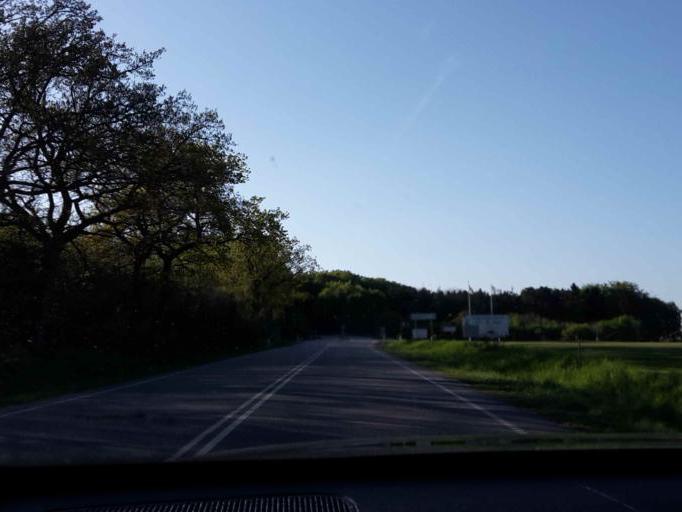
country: DK
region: Central Jutland
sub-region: Norddjurs Kommune
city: Allingabro
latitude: 56.4367
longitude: 10.3415
